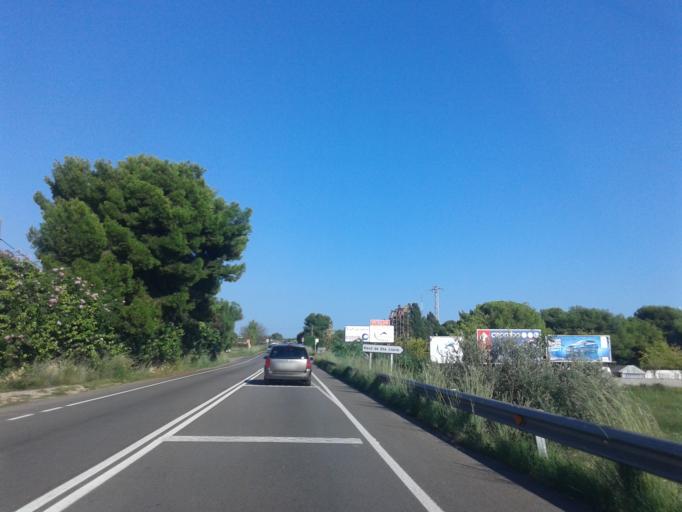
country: ES
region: Catalonia
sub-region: Provincia de Barcelona
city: Vilanova i la Geltru
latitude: 41.2109
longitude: 1.7014
